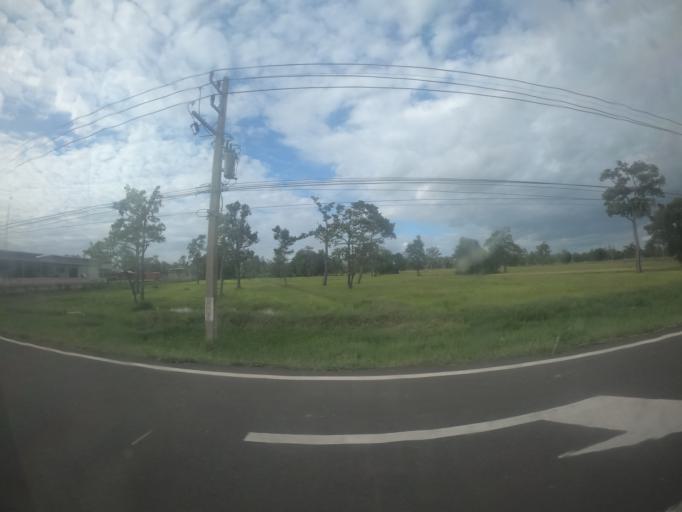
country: TH
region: Surin
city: Prasat
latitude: 14.5999
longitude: 103.4354
